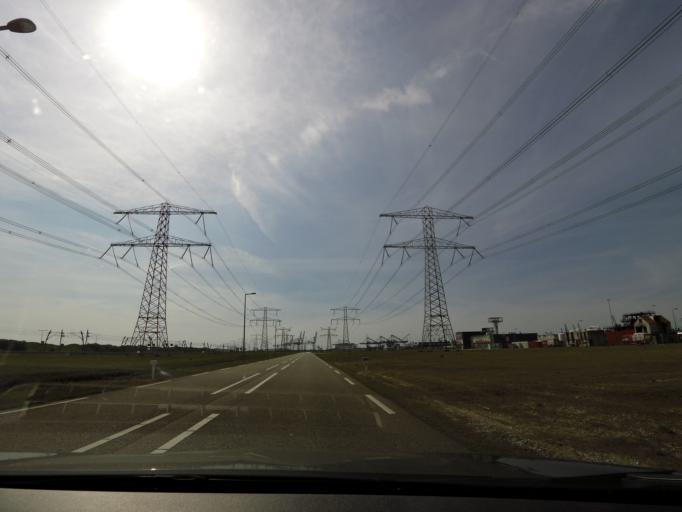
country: NL
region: South Holland
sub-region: Gemeente Rotterdam
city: Hoek van Holland
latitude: 51.9351
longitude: 4.0801
